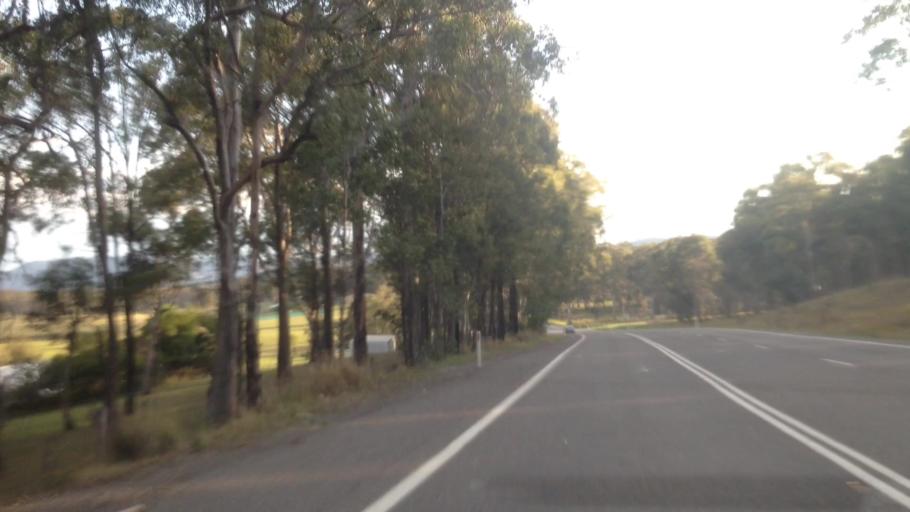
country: AU
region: New South Wales
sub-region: Cessnock
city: Kurri Kurri
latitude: -32.8615
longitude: 151.4829
